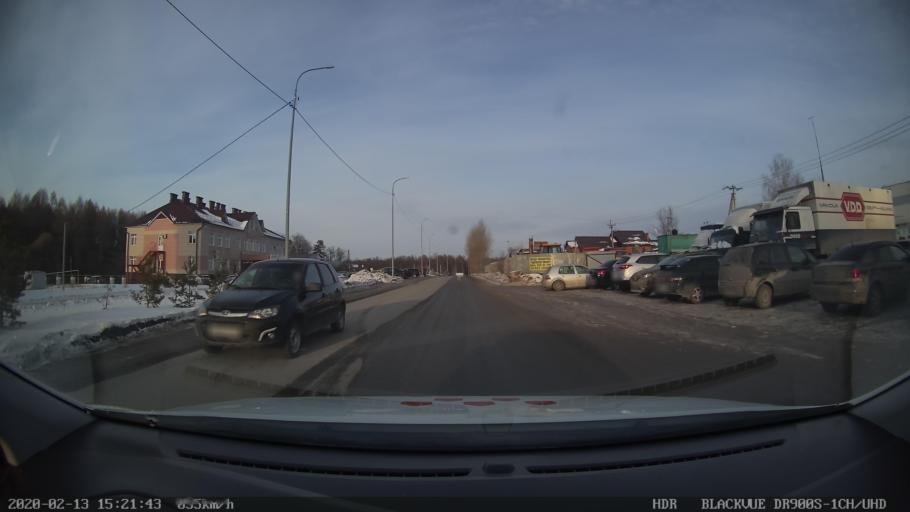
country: RU
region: Tatarstan
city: Vysokaya Gora
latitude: 55.9198
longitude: 49.3024
